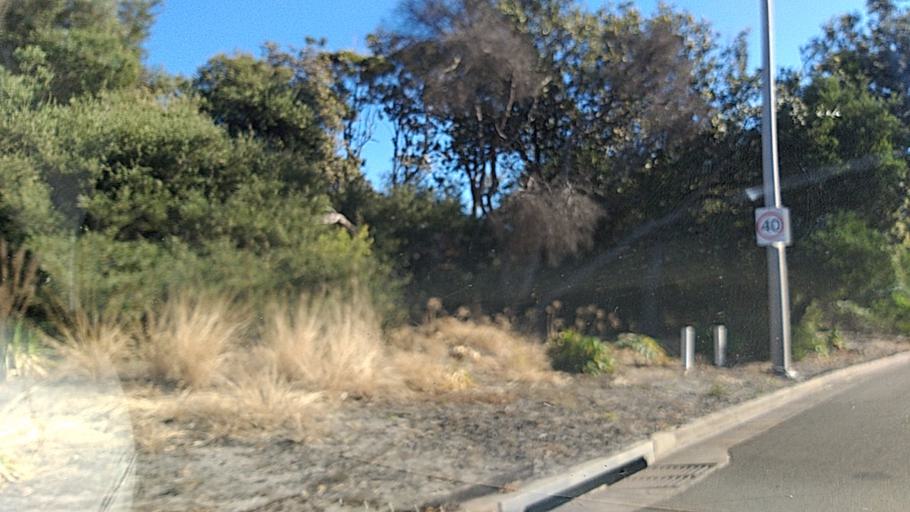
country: AU
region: New South Wales
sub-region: Wollongong
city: Coniston
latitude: -34.4440
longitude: 150.8971
